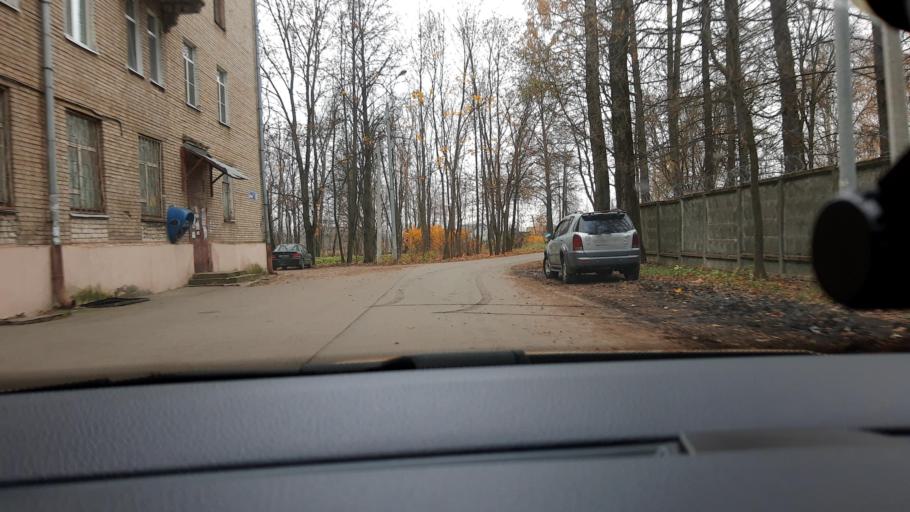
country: RU
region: Moskovskaya
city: Pirogovskiy
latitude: 55.9592
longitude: 37.7302
